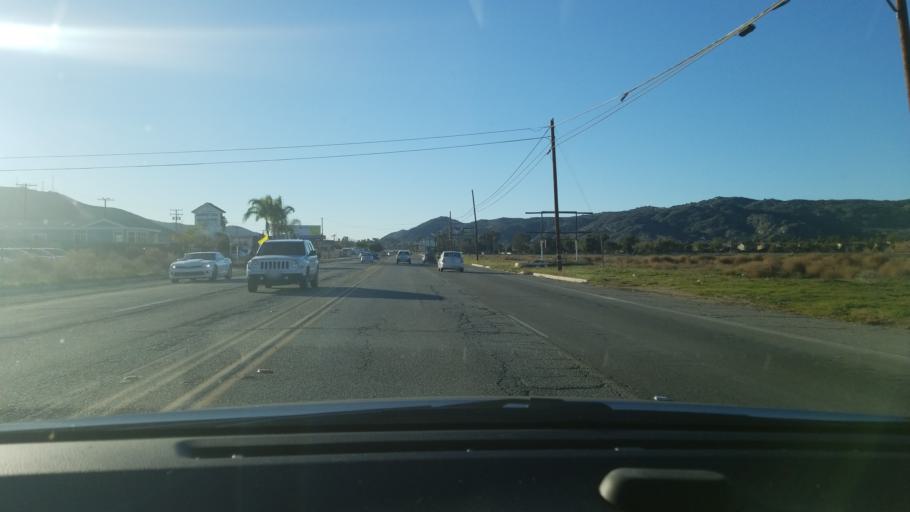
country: US
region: California
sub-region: Riverside County
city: Green Acres
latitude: 33.7439
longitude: -117.0435
